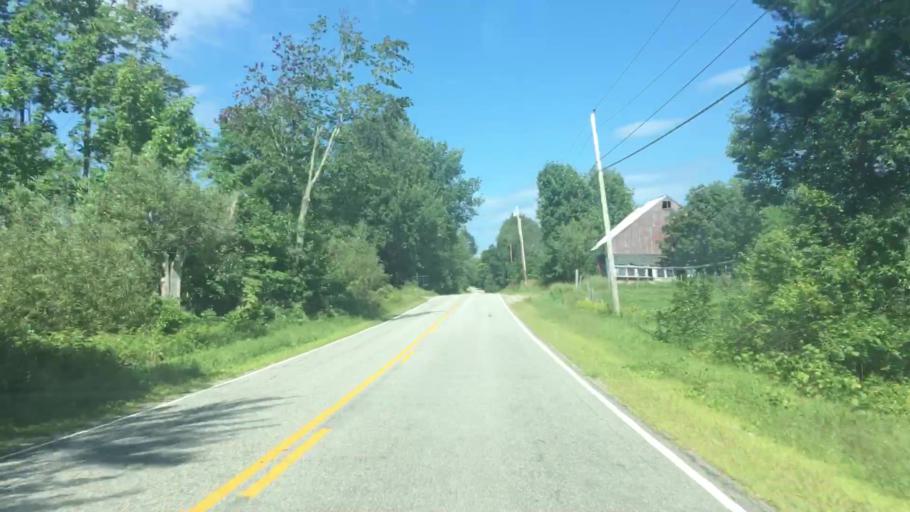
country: US
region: Maine
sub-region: Kennebec County
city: Monmouth
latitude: 44.1819
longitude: -69.9396
